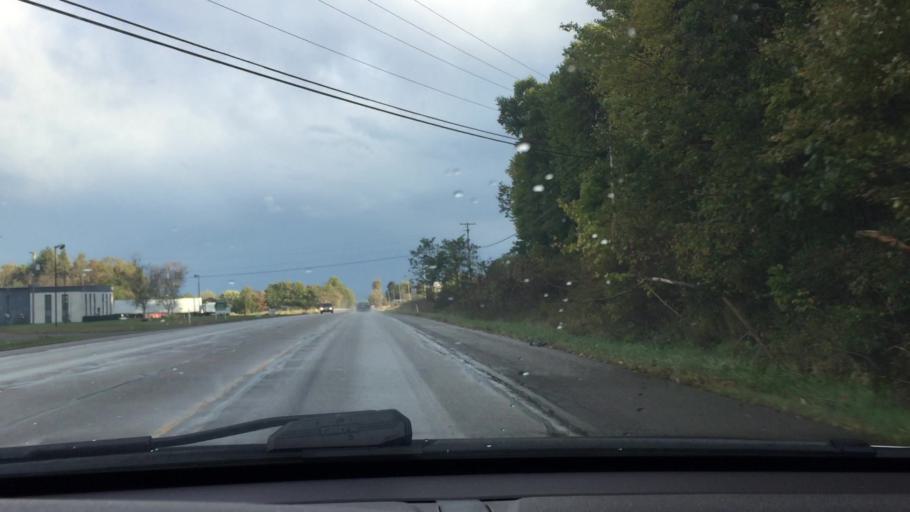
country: US
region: Ohio
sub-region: Mahoning County
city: Lowellville
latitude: 41.0600
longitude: -80.4522
